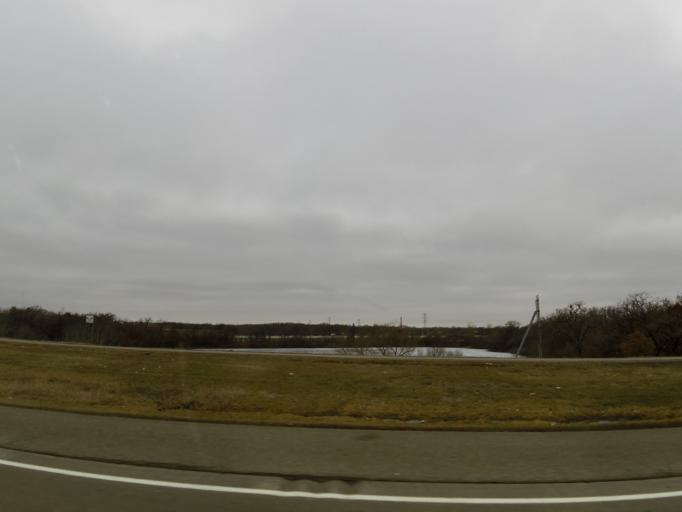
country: US
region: Minnesota
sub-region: Dakota County
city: Eagan
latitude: 44.7919
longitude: -93.2004
